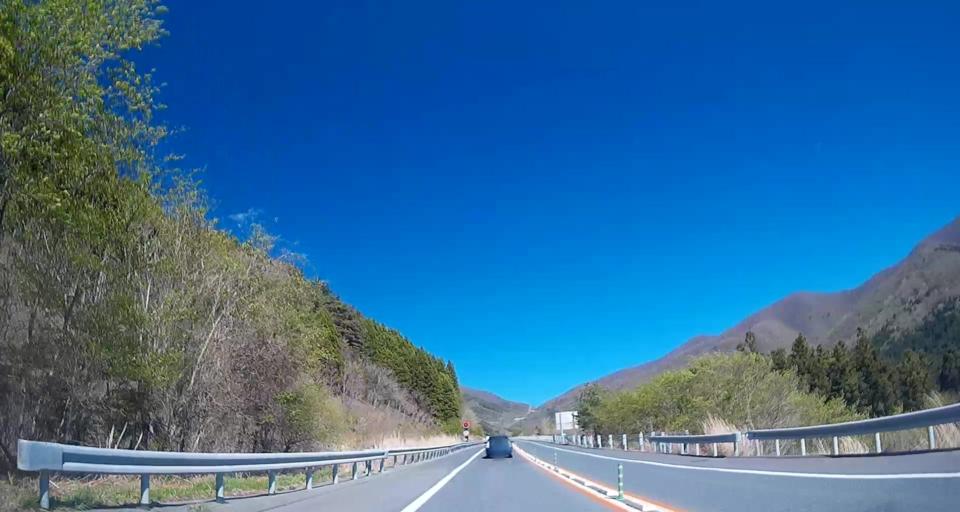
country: JP
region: Iwate
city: Ofunato
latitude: 39.1259
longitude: 141.7440
